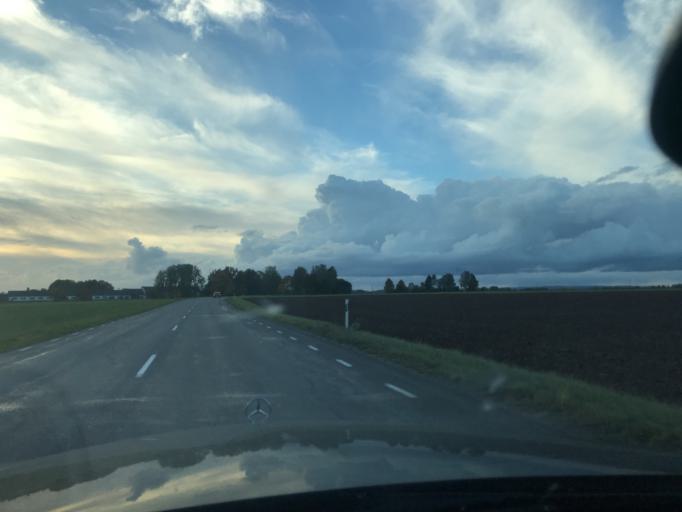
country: EE
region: Vorumaa
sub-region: Antsla vald
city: Vana-Antsla
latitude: 57.8951
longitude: 26.4924
